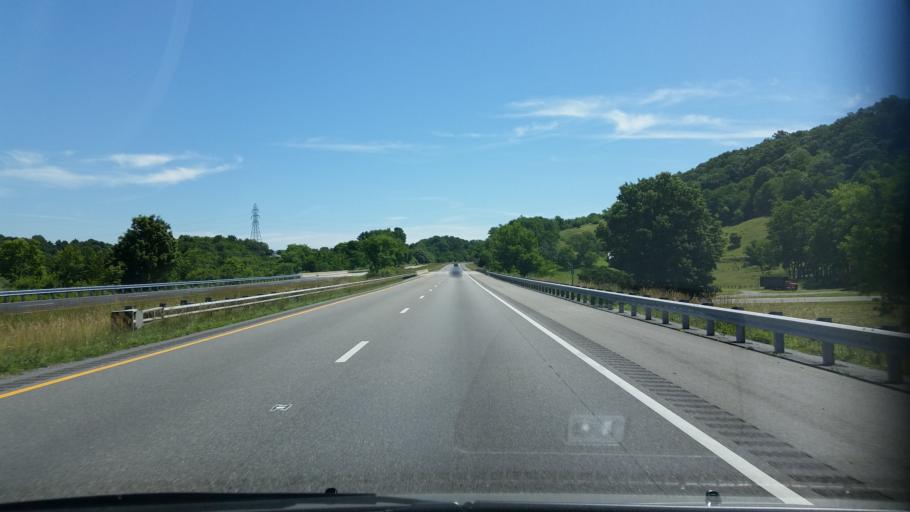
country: US
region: Virginia
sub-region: Smyth County
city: Marion
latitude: 36.8190
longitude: -81.5503
